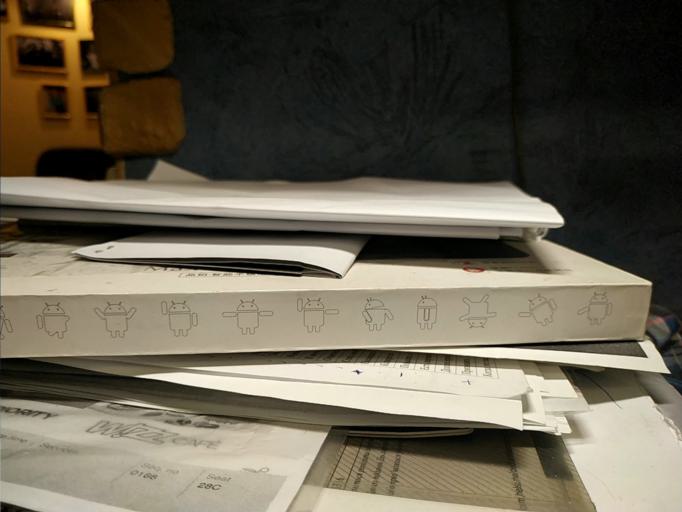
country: RU
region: Tverskaya
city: Zubtsov
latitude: 56.0834
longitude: 34.7843
